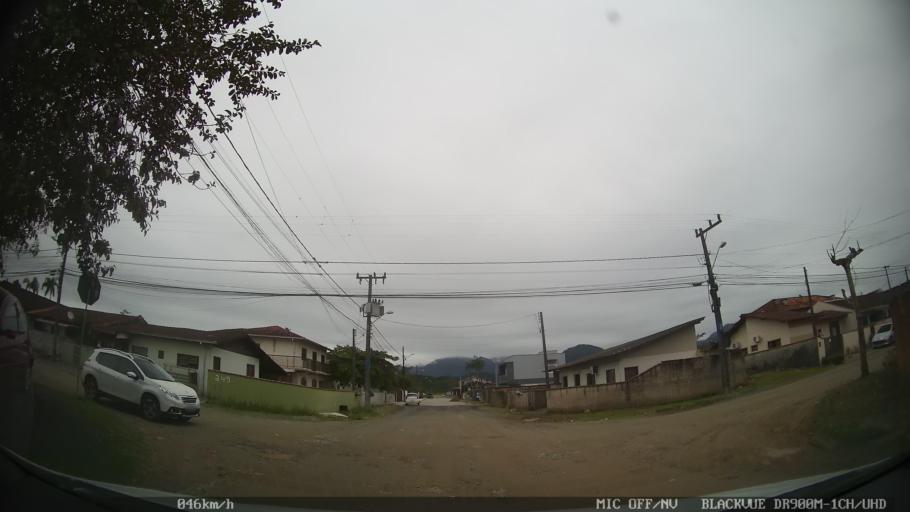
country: BR
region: Santa Catarina
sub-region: Joinville
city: Joinville
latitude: -26.2754
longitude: -48.9027
